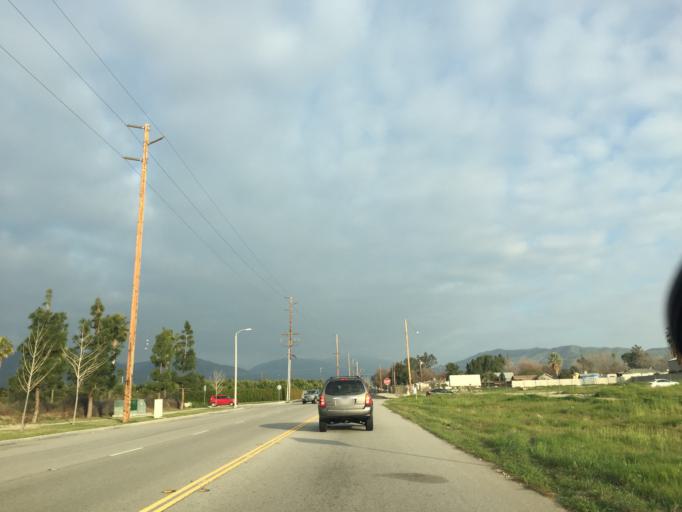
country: US
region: California
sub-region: San Bernardino County
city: Mentone
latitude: 34.0774
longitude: -117.1399
